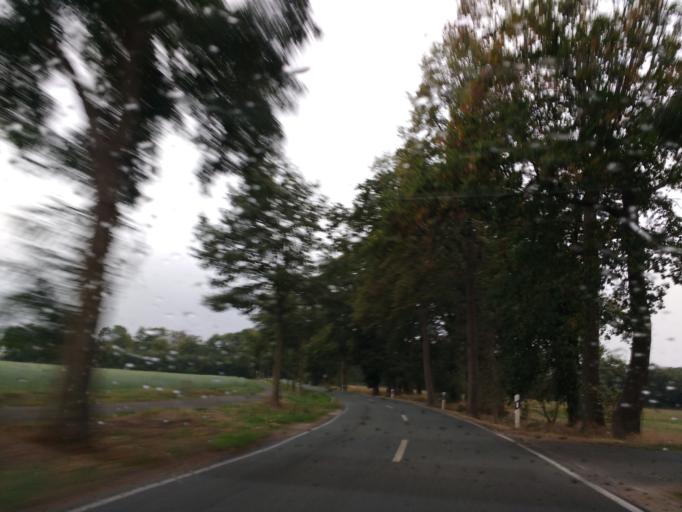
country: DE
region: North Rhine-Westphalia
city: Rietberg
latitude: 51.7357
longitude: 8.4413
